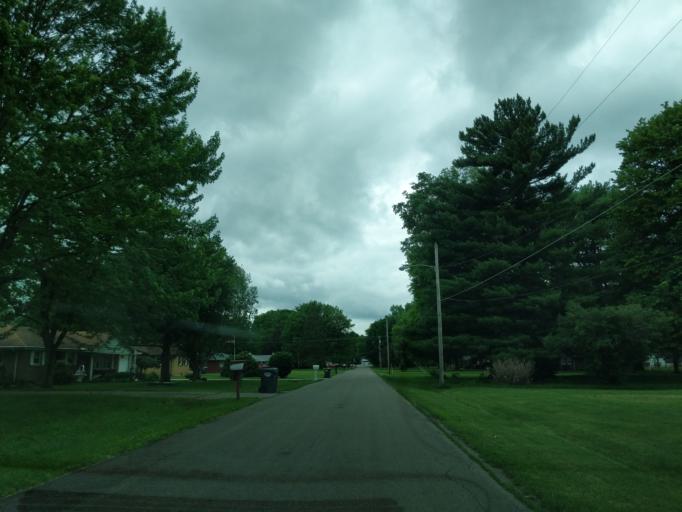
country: US
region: Indiana
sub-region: Madison County
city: Anderson
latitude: 40.0753
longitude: -85.6491
